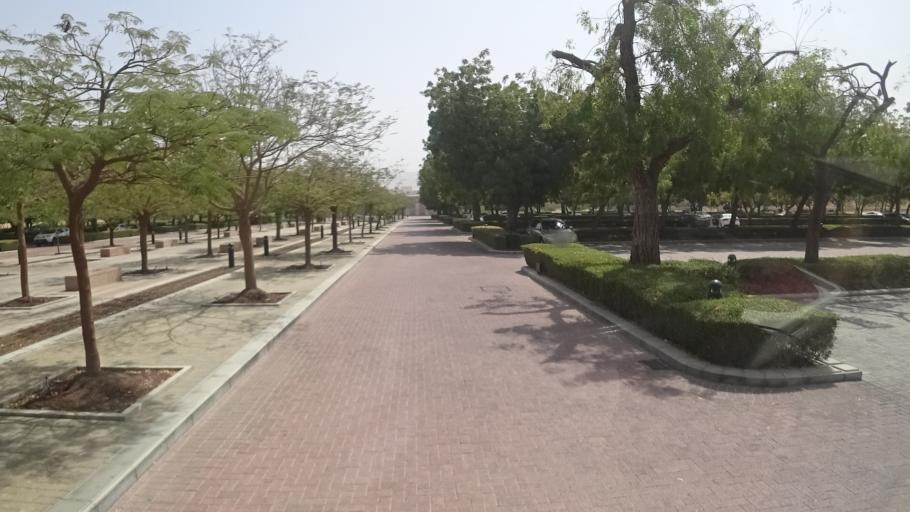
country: OM
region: Muhafazat Masqat
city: Bawshar
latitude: 23.5818
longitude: 58.3889
